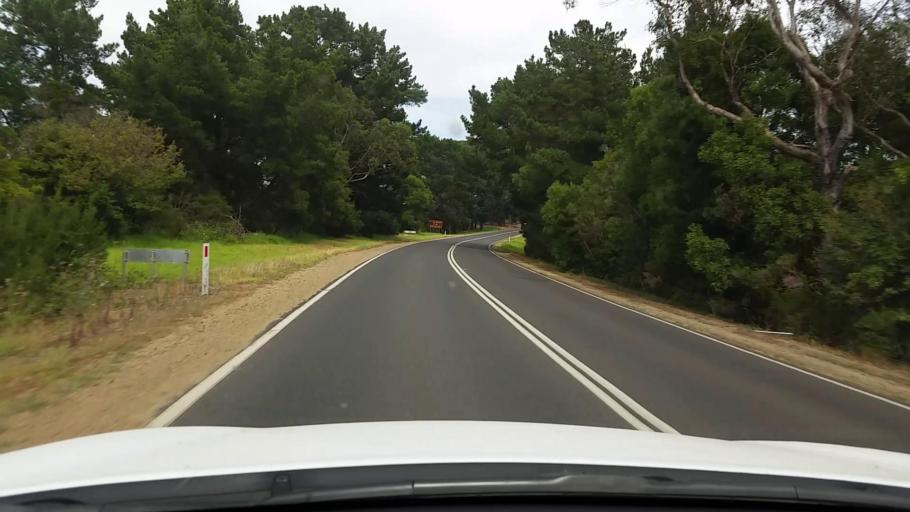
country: AU
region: Victoria
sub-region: Mornington Peninsula
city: Merricks
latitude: -38.4013
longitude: 145.0786
